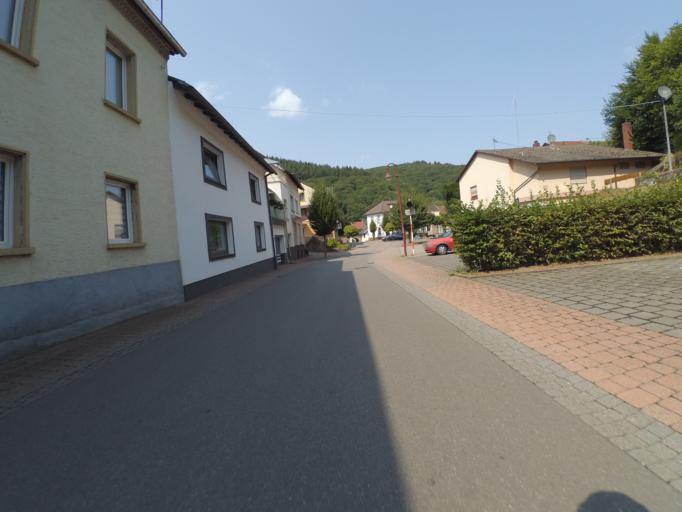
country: DE
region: Saarland
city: Saarhoelzbach
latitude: 49.5143
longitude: 6.6056
